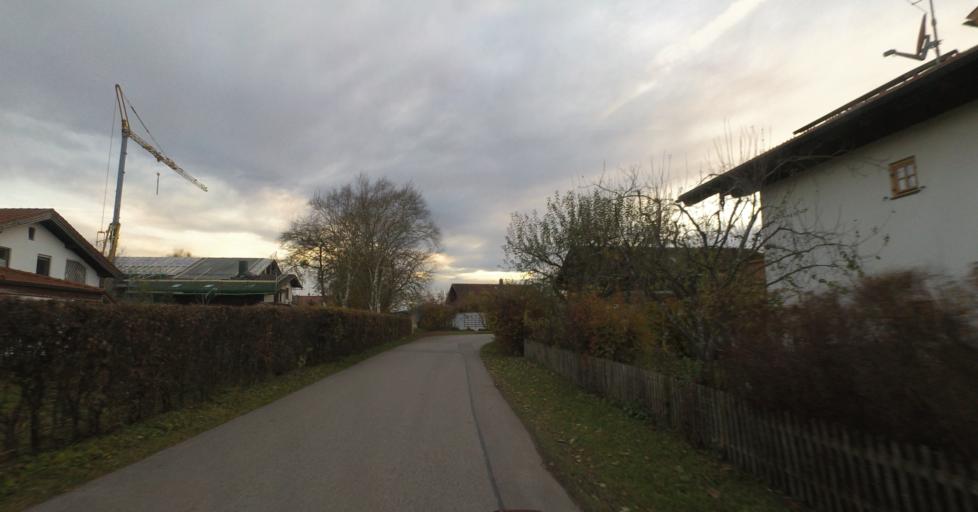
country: DE
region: Bavaria
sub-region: Upper Bavaria
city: Gstadt am Chiemsee
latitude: 47.9141
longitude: 12.4329
